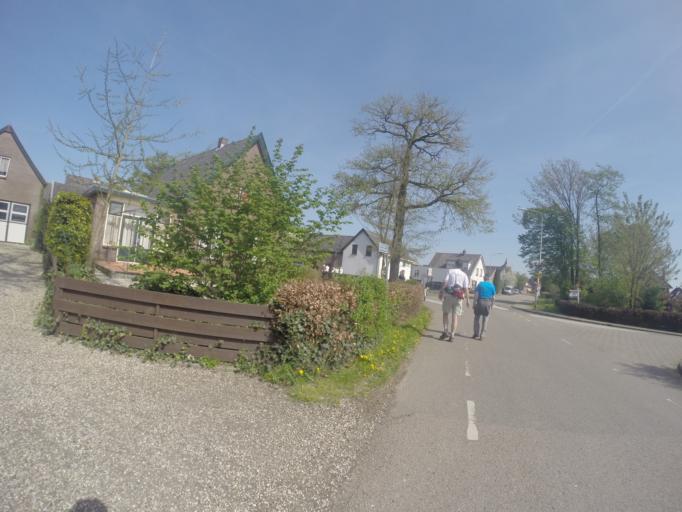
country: NL
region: Gelderland
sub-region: Gemeente Geldermalsen
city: Geldermalsen
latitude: 51.8858
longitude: 5.2429
